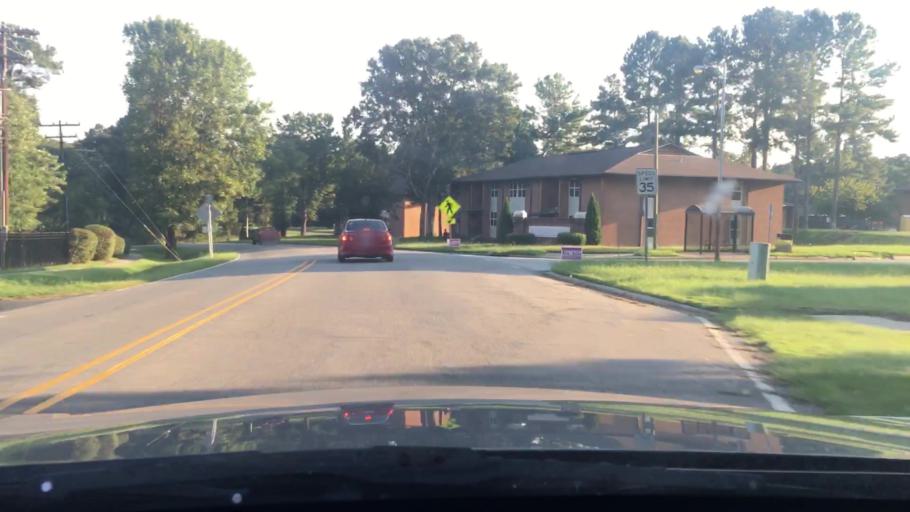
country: US
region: North Carolina
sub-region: Durham County
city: Durham
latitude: 36.0060
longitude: -78.9548
